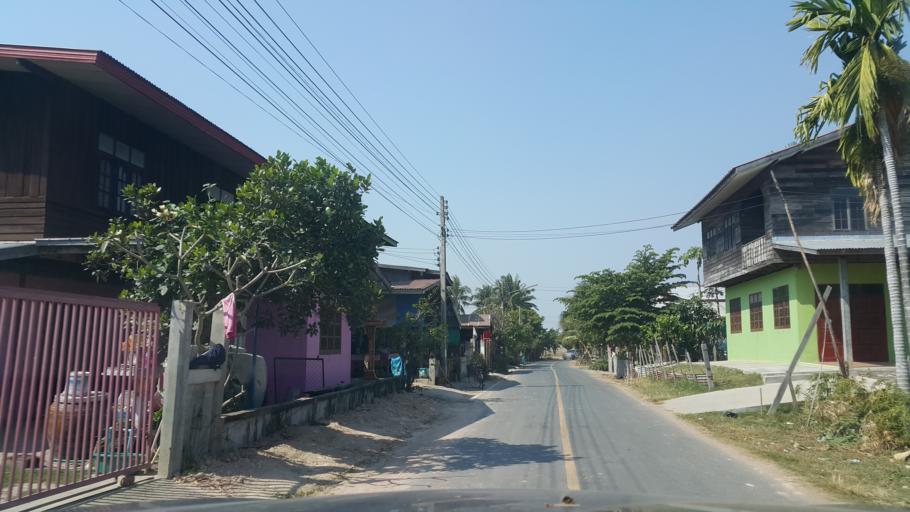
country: TH
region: Buriram
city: Krasang
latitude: 15.0890
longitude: 103.3890
